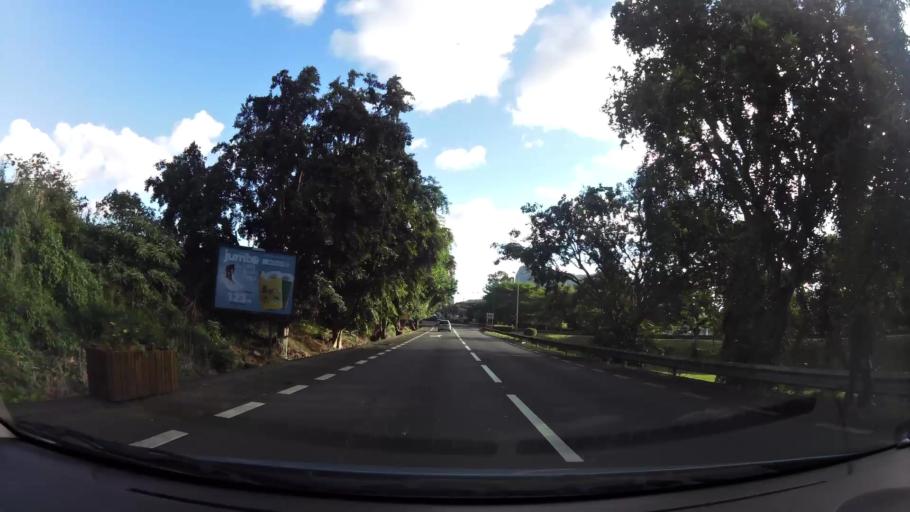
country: MU
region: Plaines Wilhems
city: Quatre Bornes
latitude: -20.2580
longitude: 57.4865
